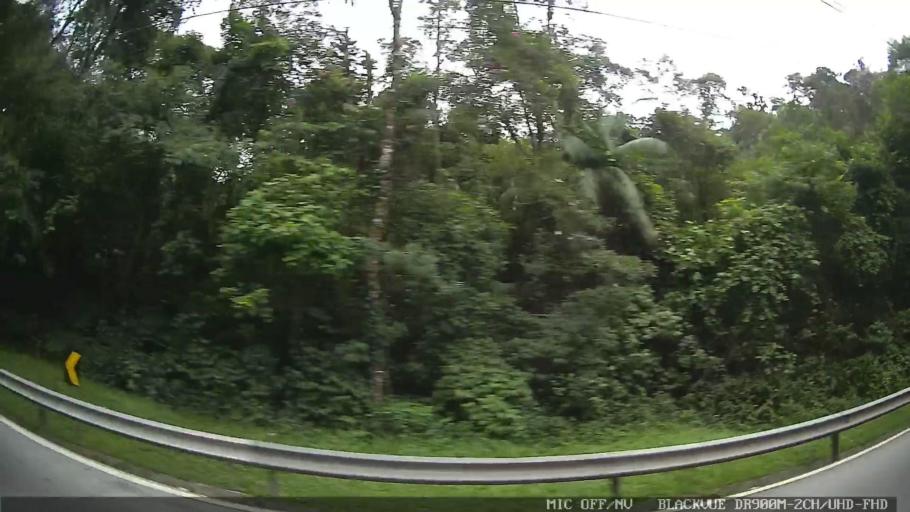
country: BR
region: Sao Paulo
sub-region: Caraguatatuba
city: Caraguatatuba
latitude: -23.5916
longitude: -45.4541
